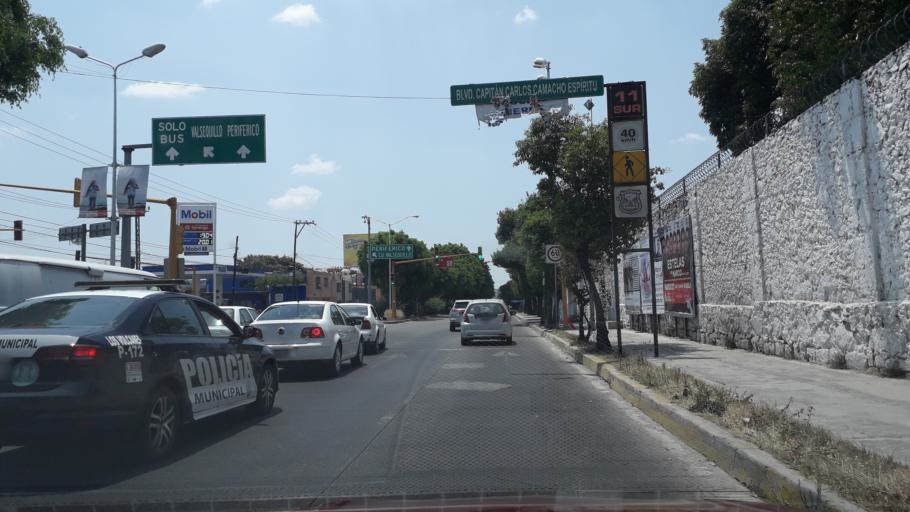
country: MX
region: Puebla
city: Puebla
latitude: 19.0329
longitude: -98.2159
